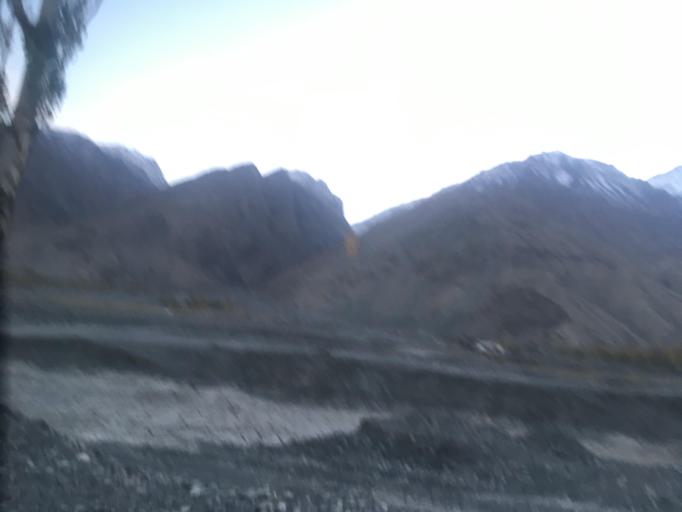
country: PK
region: Gilgit-Baltistan
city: Skardu
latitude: 35.3022
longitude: 75.5392
